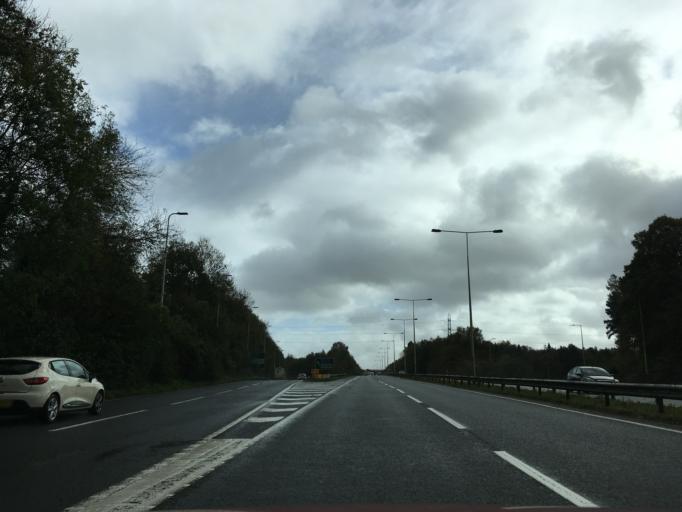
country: GB
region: Wales
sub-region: Cardiff
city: Radyr
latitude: 51.5286
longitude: -3.2487
